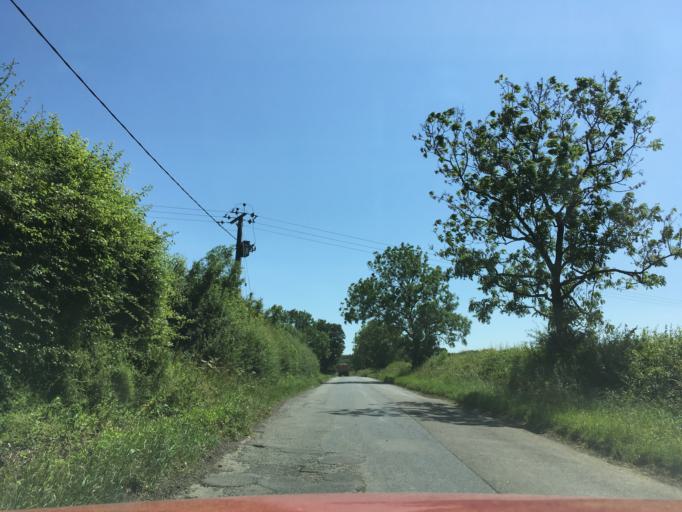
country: GB
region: England
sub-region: Northamptonshire
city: Deanshanger
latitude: 52.0084
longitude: -0.8943
